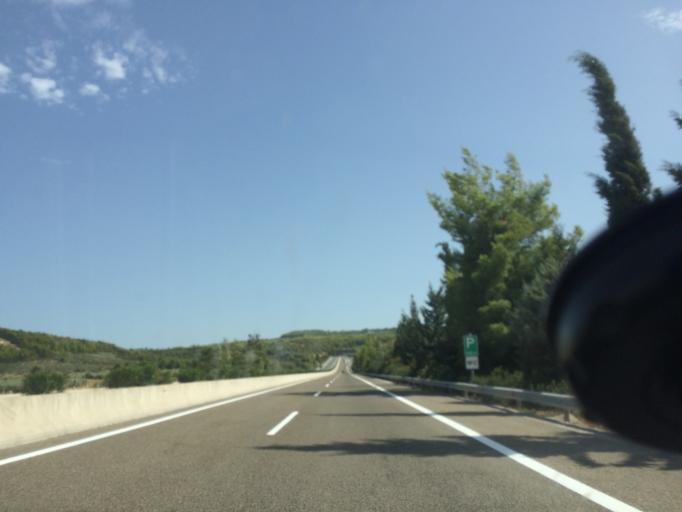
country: GR
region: Central Greece
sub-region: Nomos Fthiotidos
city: Martinon
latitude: 38.6151
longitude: 23.1538
